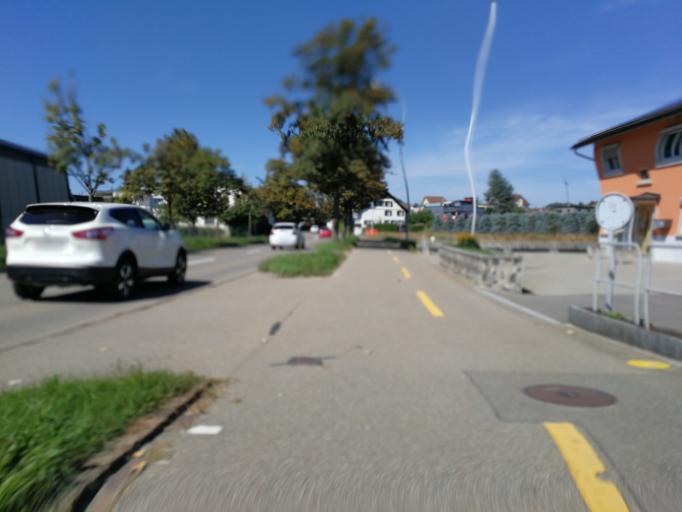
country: CH
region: Zurich
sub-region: Bezirk Pfaeffikon
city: Pfaeffikon / Irgenhausen
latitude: 47.3587
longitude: 8.7955
